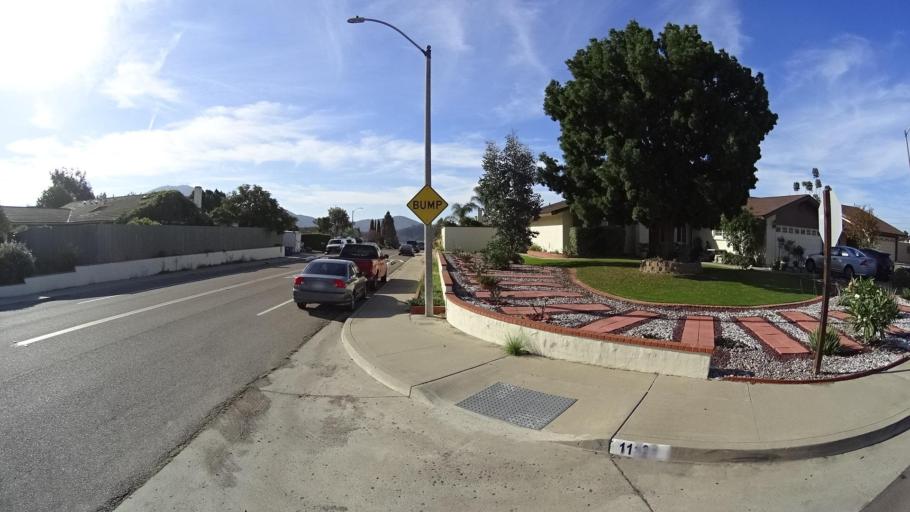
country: US
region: California
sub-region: San Diego County
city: Casa de Oro-Mount Helix
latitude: 32.7382
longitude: -116.9611
